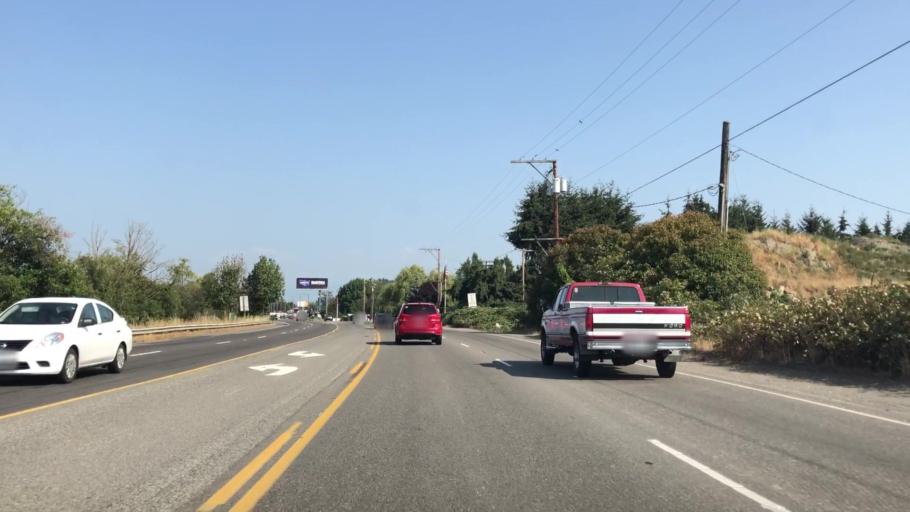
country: US
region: Washington
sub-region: Pierce County
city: Waller
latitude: 47.2113
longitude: -122.3378
